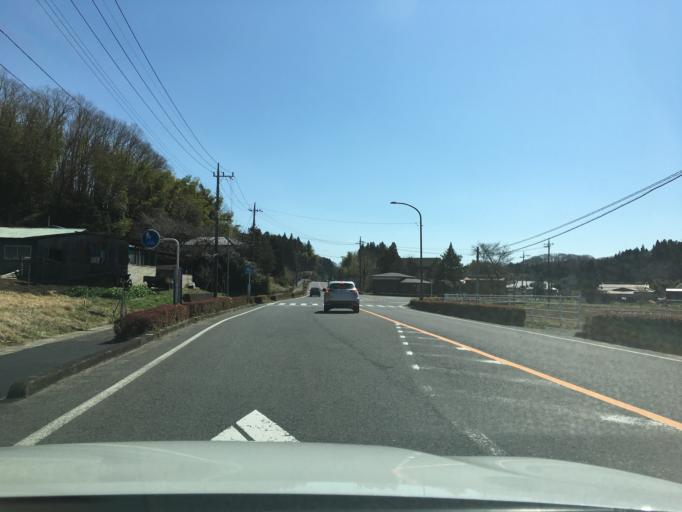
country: JP
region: Tochigi
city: Kuroiso
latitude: 37.0417
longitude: 140.1706
